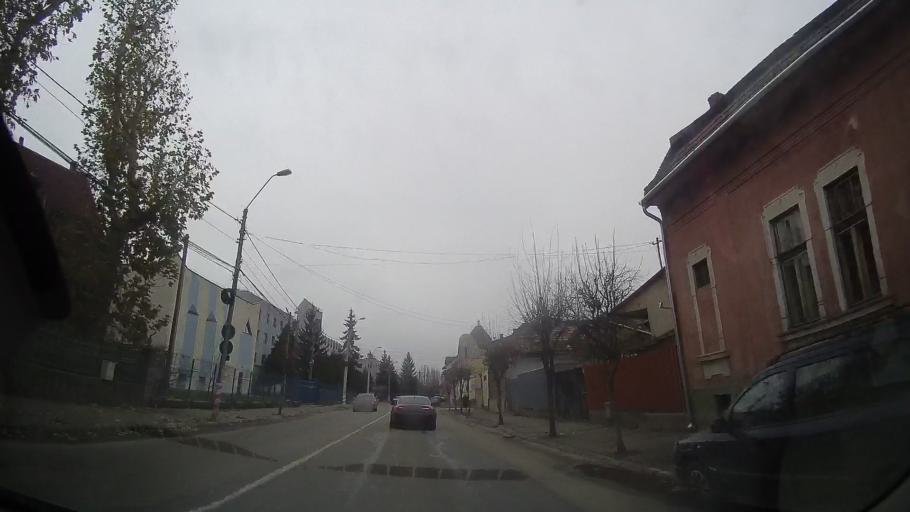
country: RO
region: Mures
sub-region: Comuna Santana de Mures
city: Santana de Mures
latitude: 46.5562
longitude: 24.5474
